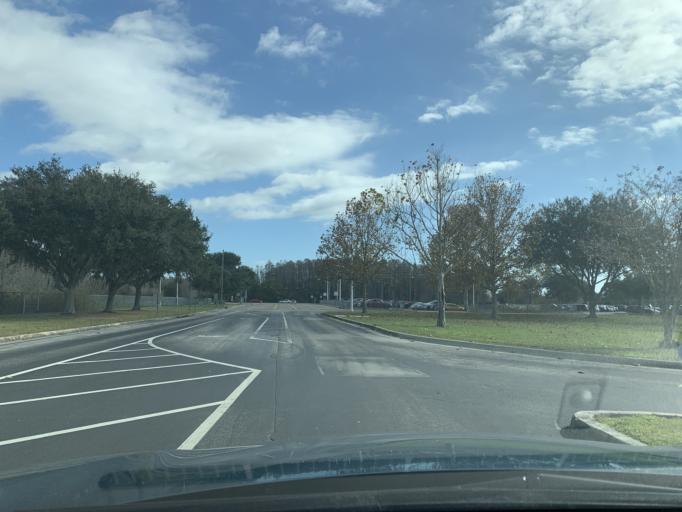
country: US
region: Florida
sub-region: Pasco County
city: Trinity
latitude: 28.1948
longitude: -82.6687
